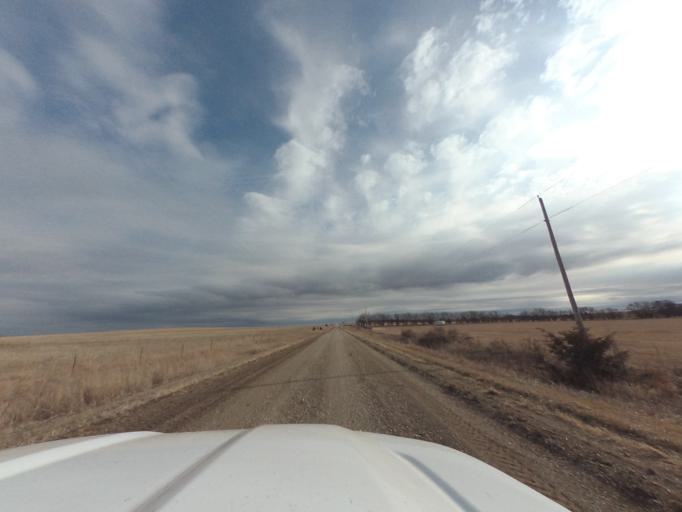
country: US
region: Kansas
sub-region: Chase County
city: Cottonwood Falls
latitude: 38.2170
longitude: -96.6883
